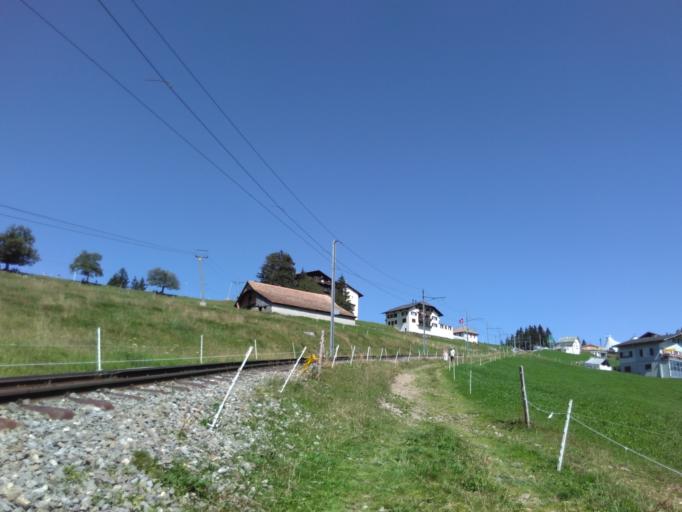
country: CH
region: Lucerne
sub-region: Lucerne-Land District
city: Vitznau
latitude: 47.0502
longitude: 8.4723
